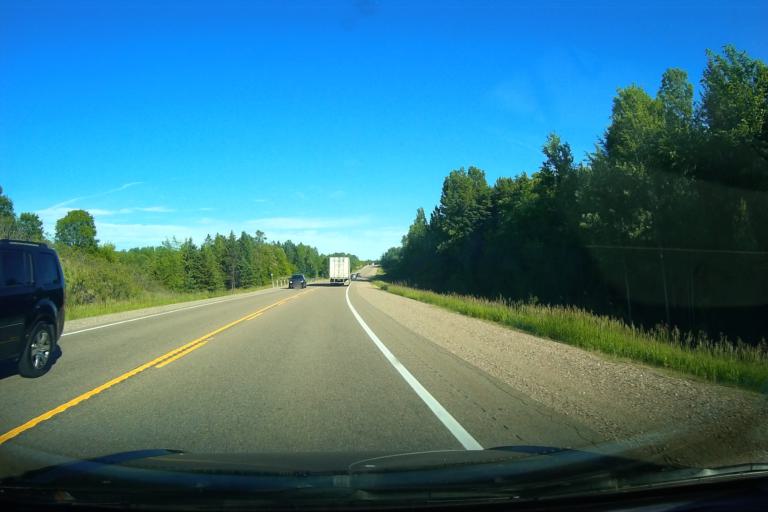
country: CA
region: Ontario
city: Renfrew
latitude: 45.5636
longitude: -76.7536
